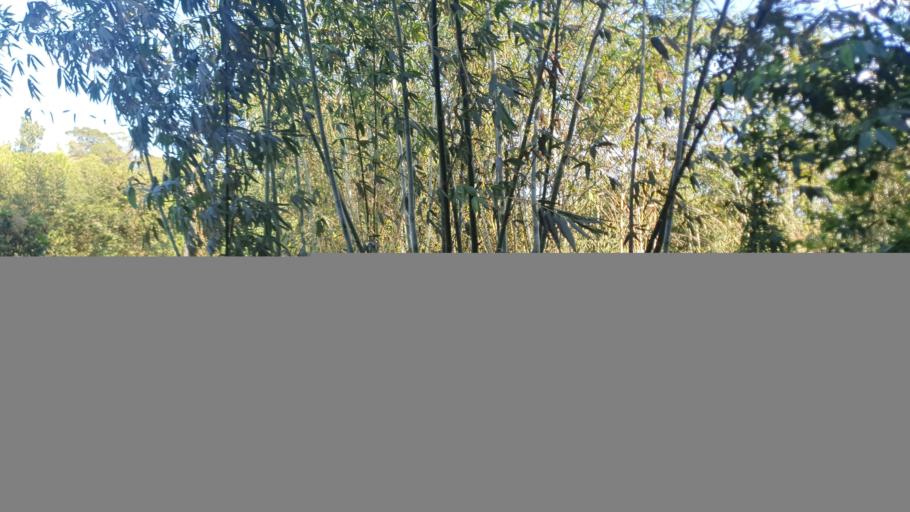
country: TW
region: Taiwan
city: Yujing
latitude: 23.0157
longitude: 120.3845
